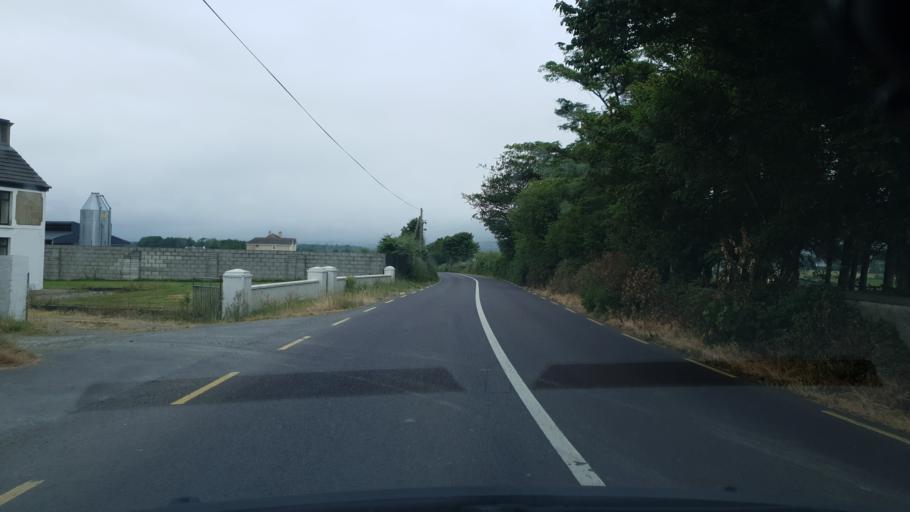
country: IE
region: Munster
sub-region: Ciarrai
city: Tralee
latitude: 52.1619
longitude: -9.6918
